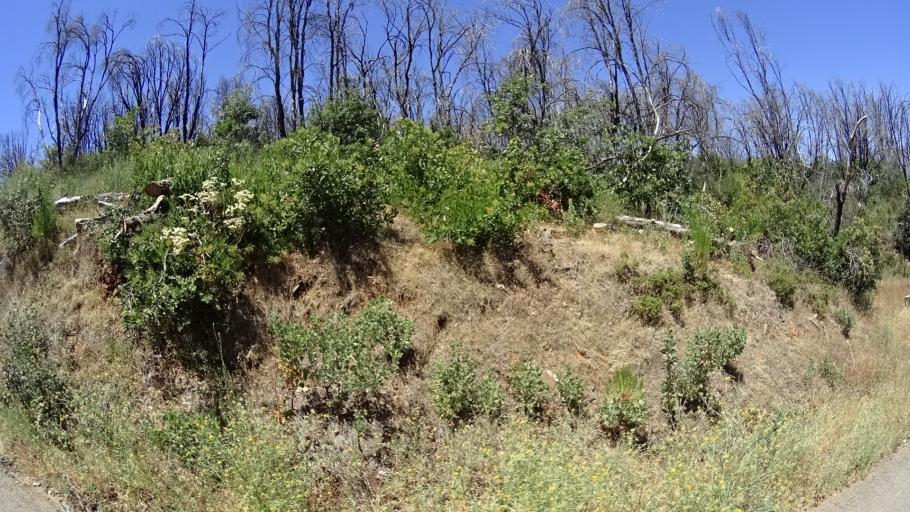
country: US
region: California
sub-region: Calaveras County
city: Mountain Ranch
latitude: 38.2299
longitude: -120.5894
